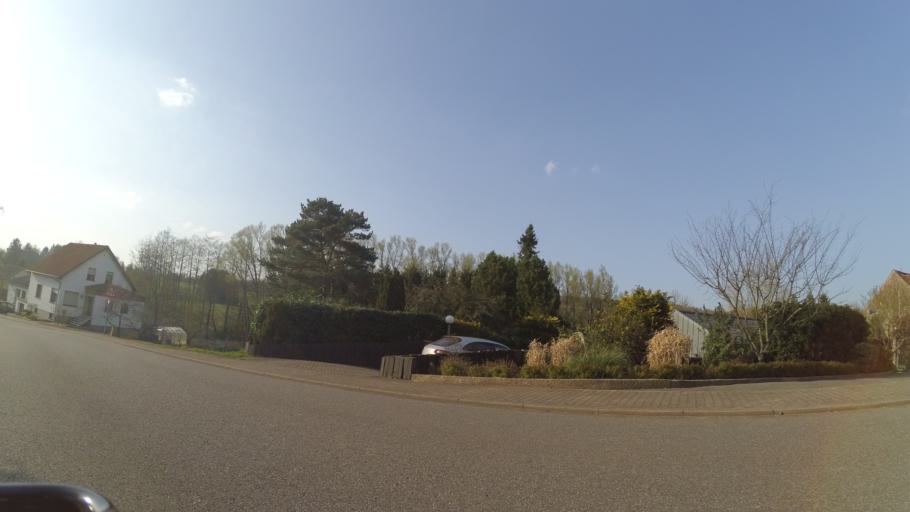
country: DE
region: Saarland
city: Heusweiler
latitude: 49.3477
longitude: 6.9708
